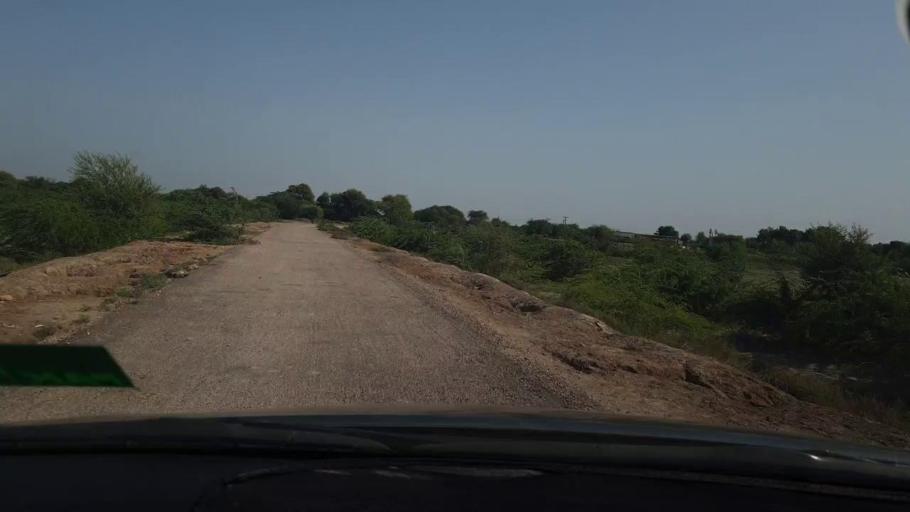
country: PK
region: Sindh
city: Naukot
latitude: 24.9464
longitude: 69.2473
